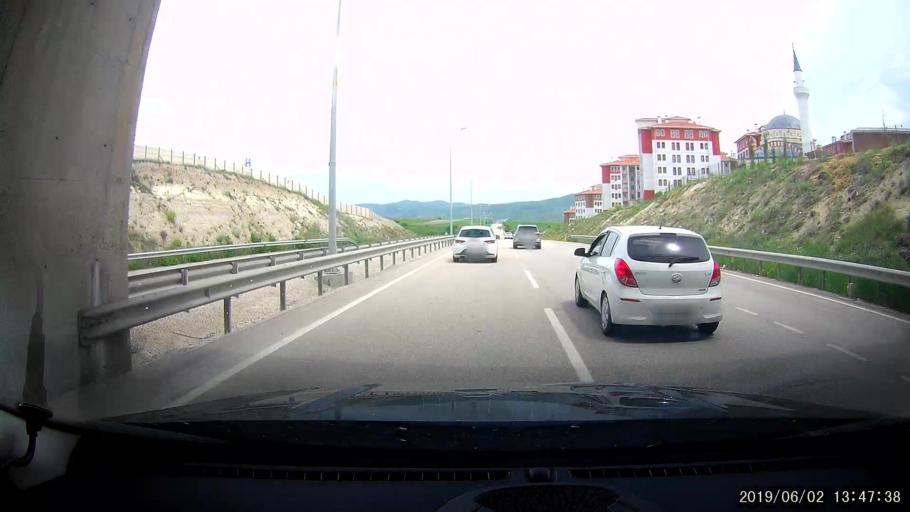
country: TR
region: Cankiri
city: Kursunlu
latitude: 40.8393
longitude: 33.2870
